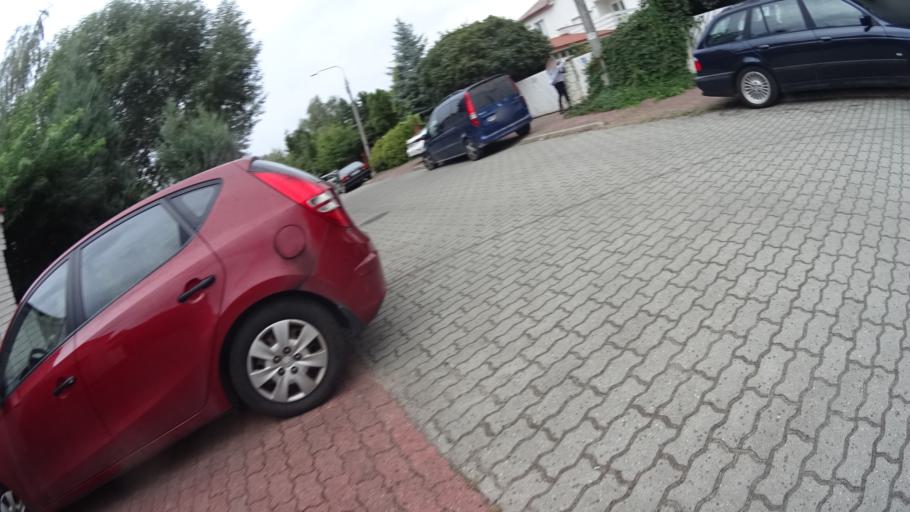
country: PL
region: Masovian Voivodeship
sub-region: Powiat pruszkowski
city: Nadarzyn
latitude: 52.1076
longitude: 20.7981
